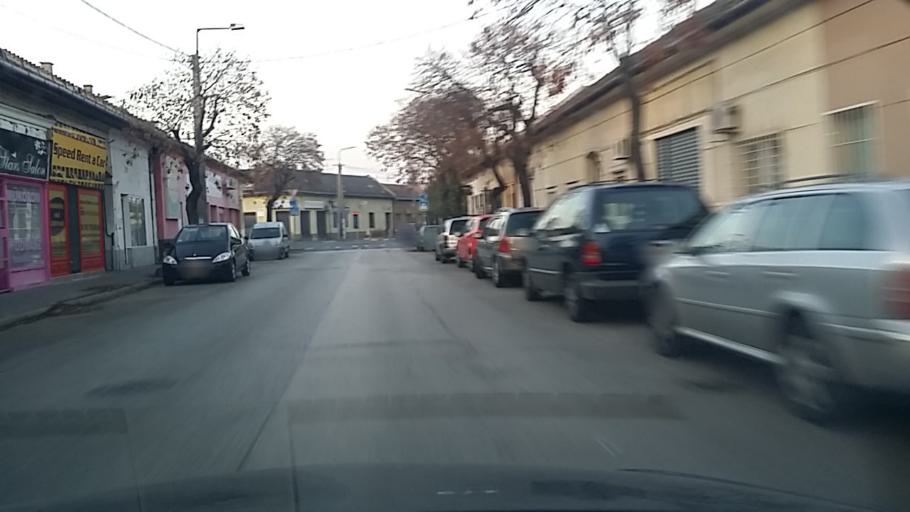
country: HU
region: Budapest
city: Budapest IV. keruelet
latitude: 47.5649
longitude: 19.0881
